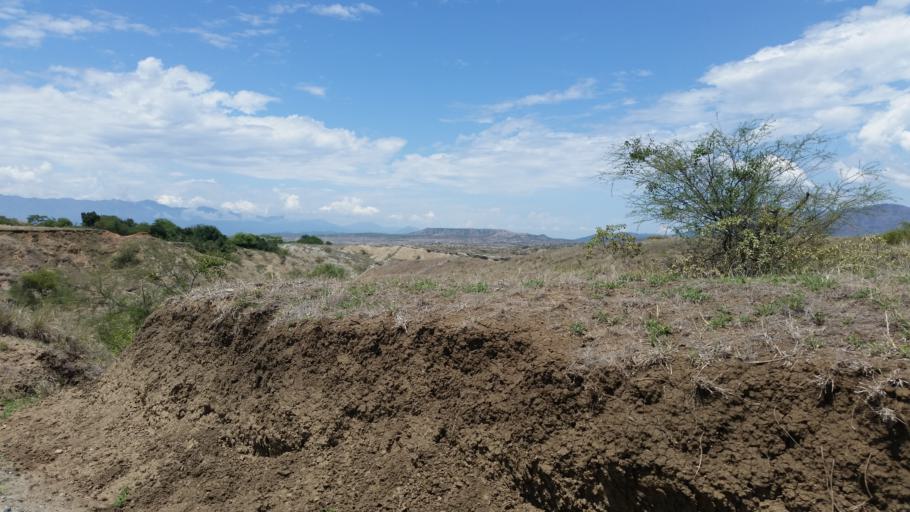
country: CO
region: Huila
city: Baraya
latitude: 3.2367
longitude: -75.1053
